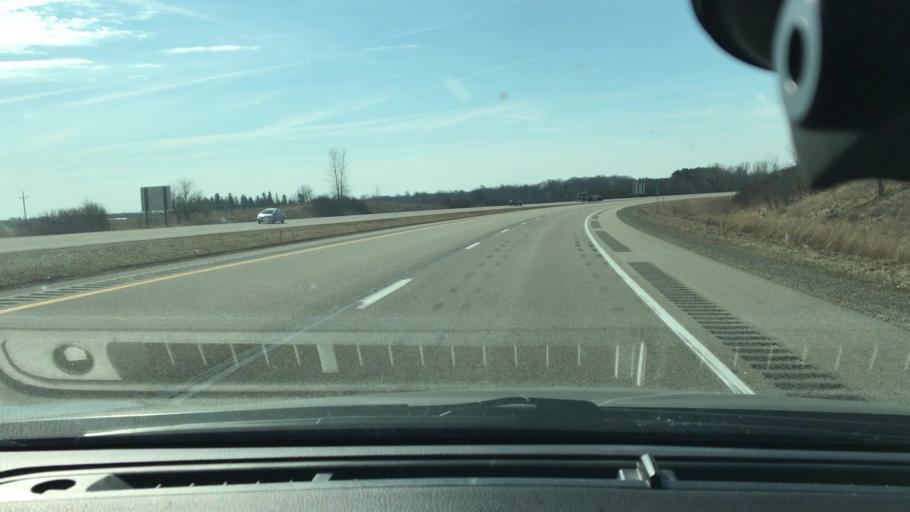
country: US
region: Iowa
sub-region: Floyd County
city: Charles City
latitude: 43.0351
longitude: -92.6521
